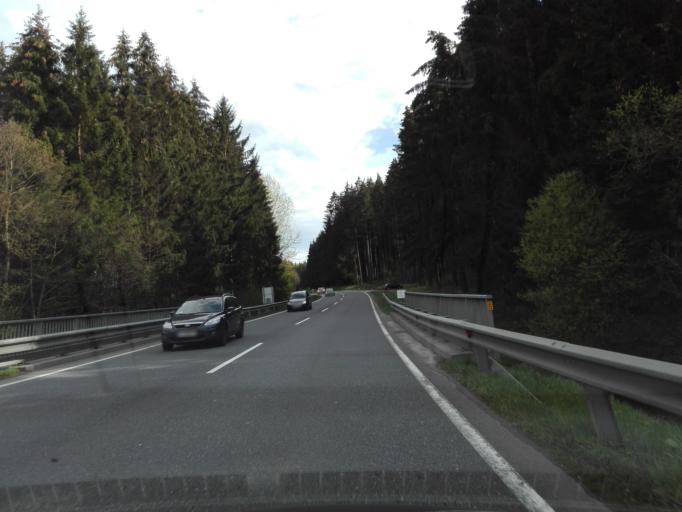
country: AT
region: Upper Austria
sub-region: Politischer Bezirk Rohrbach
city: Kleinzell im Muehlkreis
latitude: 48.4560
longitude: 14.0329
